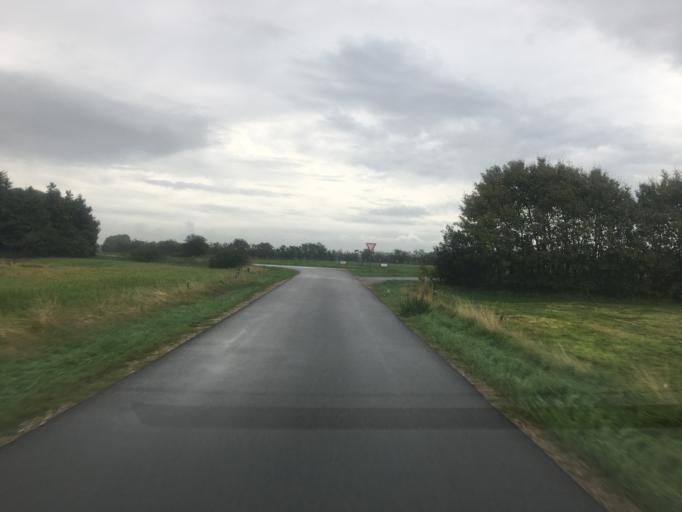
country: DK
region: South Denmark
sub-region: Tonder Kommune
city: Logumkloster
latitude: 54.9921
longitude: 9.0017
